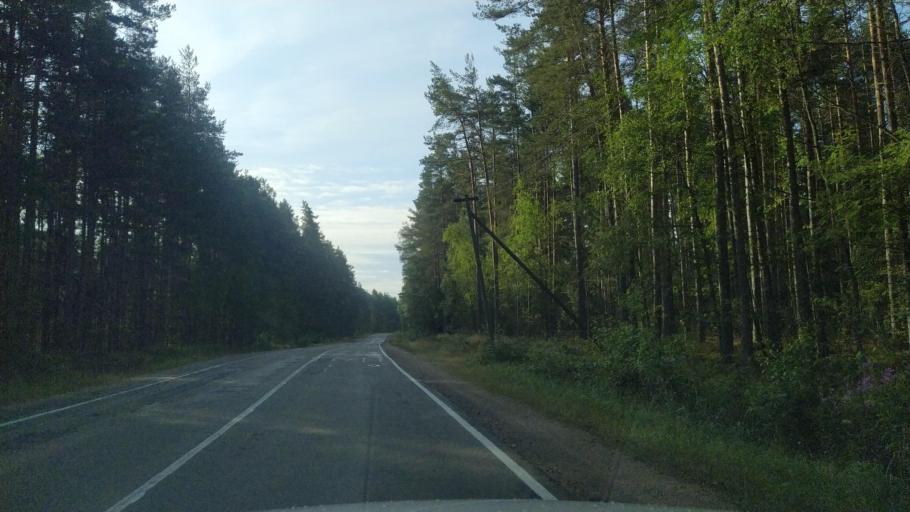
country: RU
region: Leningrad
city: Priozersk
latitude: 61.0001
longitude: 30.2434
